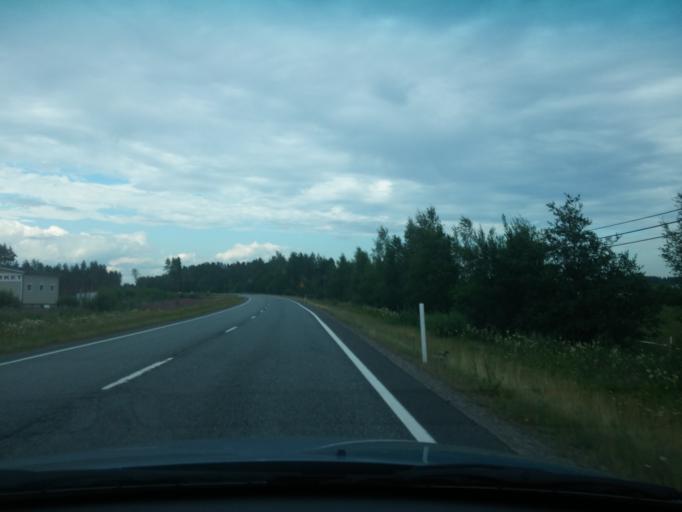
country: FI
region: Haeme
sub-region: Haemeenlinna
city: Tervakoski
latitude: 60.7402
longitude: 24.6250
